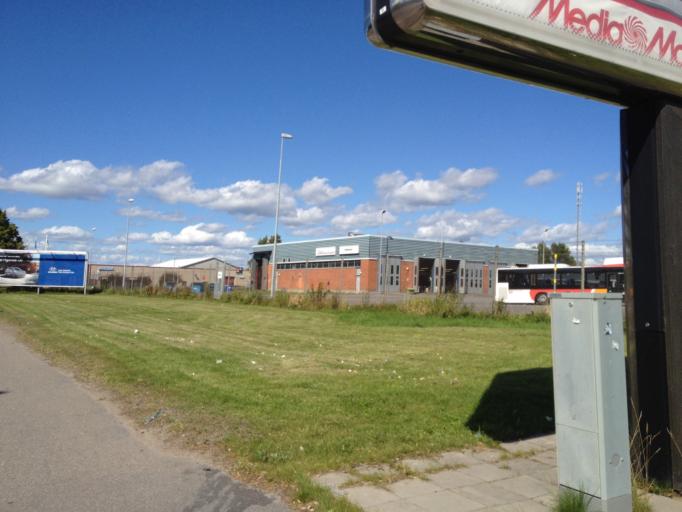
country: SE
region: OEstergoetland
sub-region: Norrkopings Kommun
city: Norrkoping
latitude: 58.6000
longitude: 16.1891
